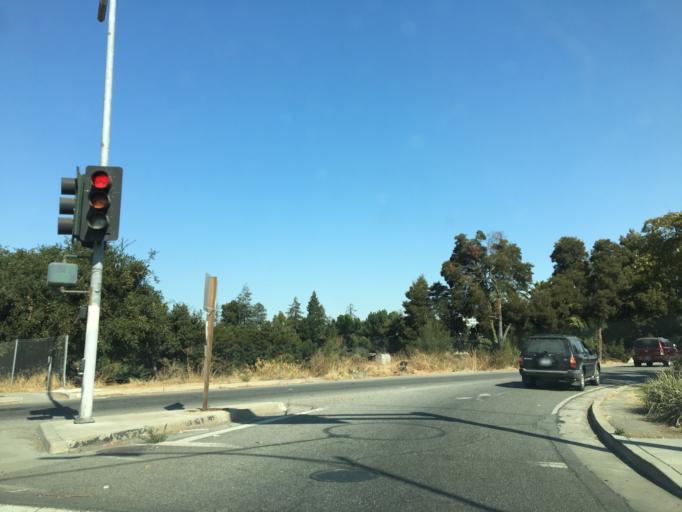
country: US
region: California
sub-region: Santa Clara County
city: San Jose
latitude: 37.3216
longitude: -121.8976
